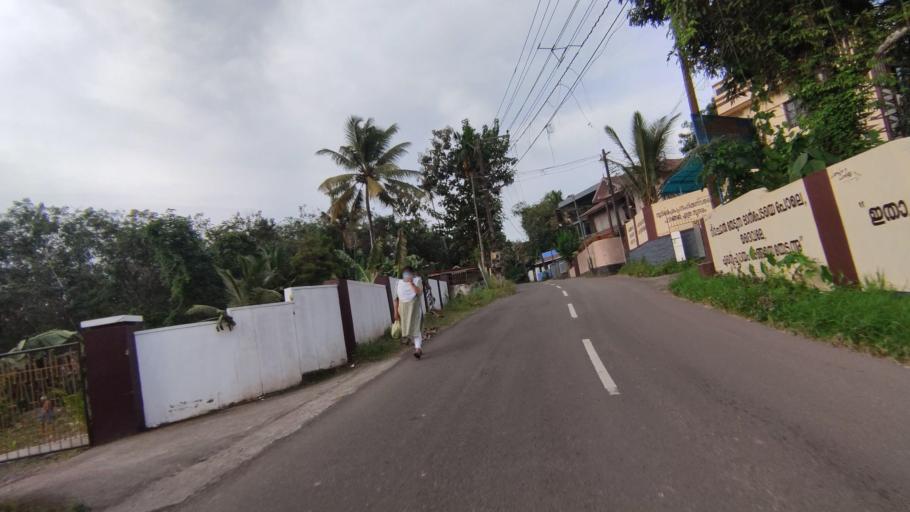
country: IN
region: Kerala
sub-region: Kottayam
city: Kottayam
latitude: 9.6415
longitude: 76.5176
